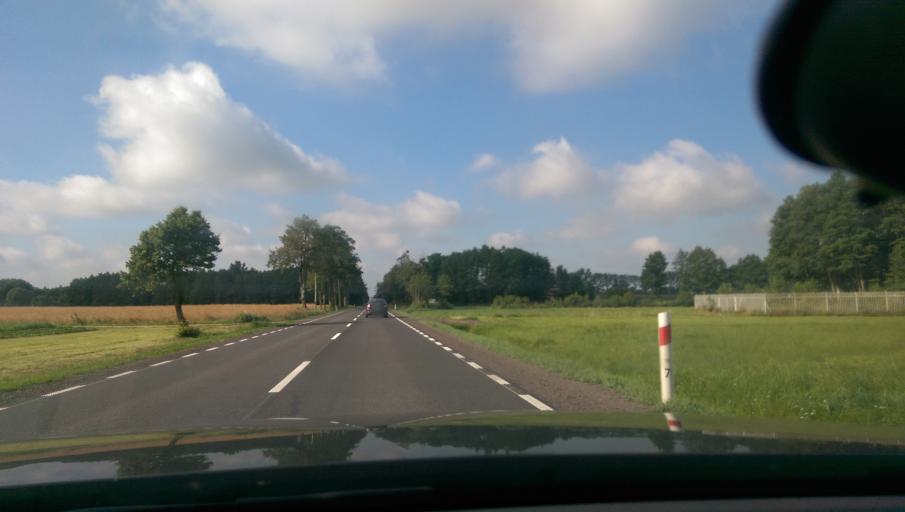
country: PL
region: Masovian Voivodeship
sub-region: Powiat ciechanowski
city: Ojrzen
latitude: 52.7302
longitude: 20.5137
